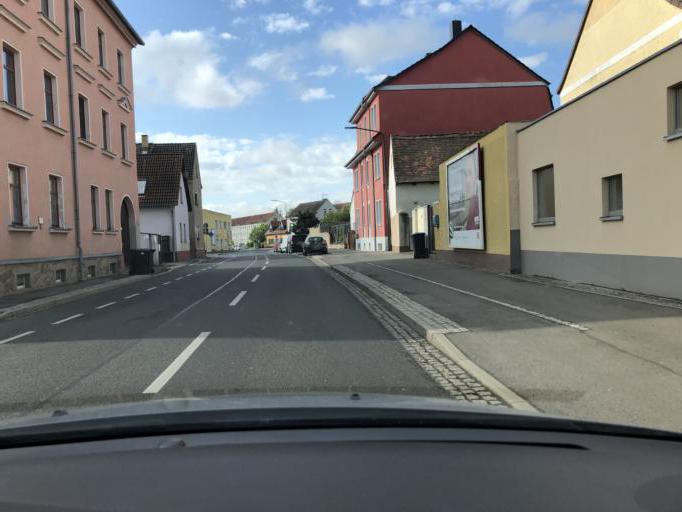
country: DE
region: Saxony
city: Markkleeberg
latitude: 51.2606
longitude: 12.3784
